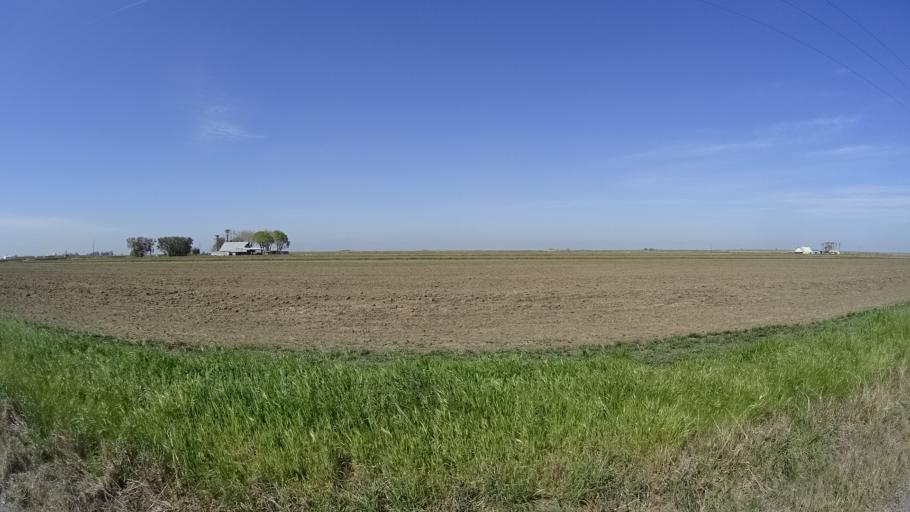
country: US
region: California
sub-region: Glenn County
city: Hamilton City
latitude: 39.6106
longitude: -122.0743
